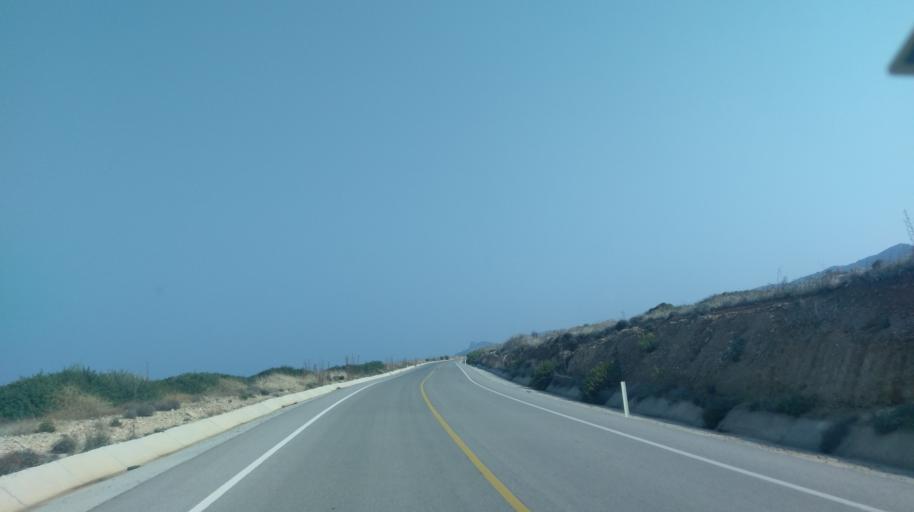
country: CY
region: Ammochostos
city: Trikomo
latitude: 35.4425
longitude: 33.9654
